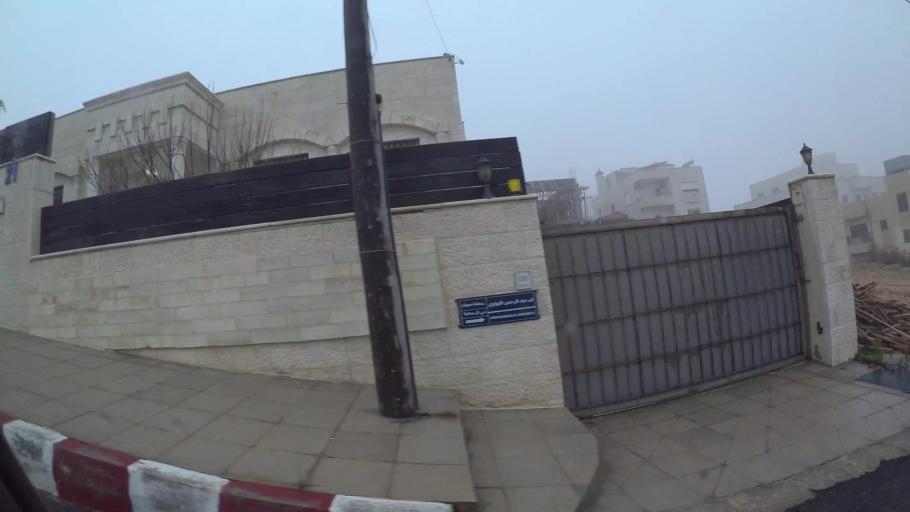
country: JO
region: Amman
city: Al Jubayhah
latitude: 32.0140
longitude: 35.8381
